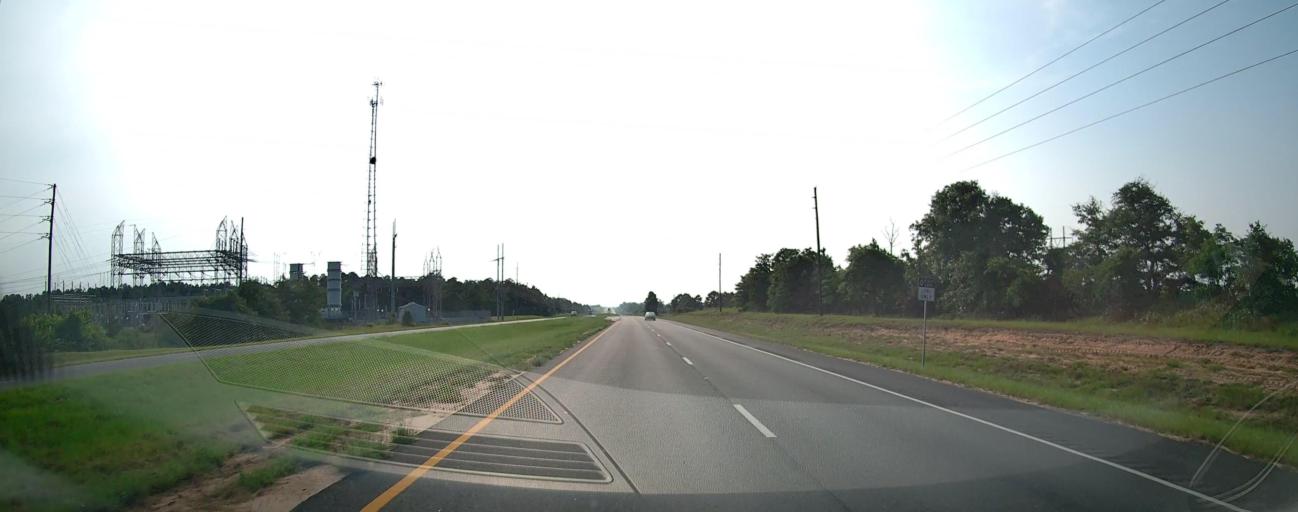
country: US
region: Georgia
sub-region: Taylor County
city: Butler
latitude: 32.5714
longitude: -84.2878
